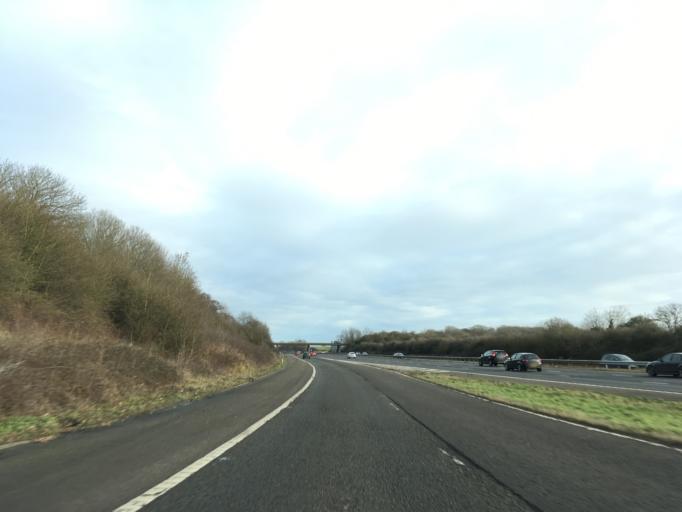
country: GB
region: England
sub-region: Gloucestershire
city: Stonehouse
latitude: 51.7613
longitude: -2.3212
